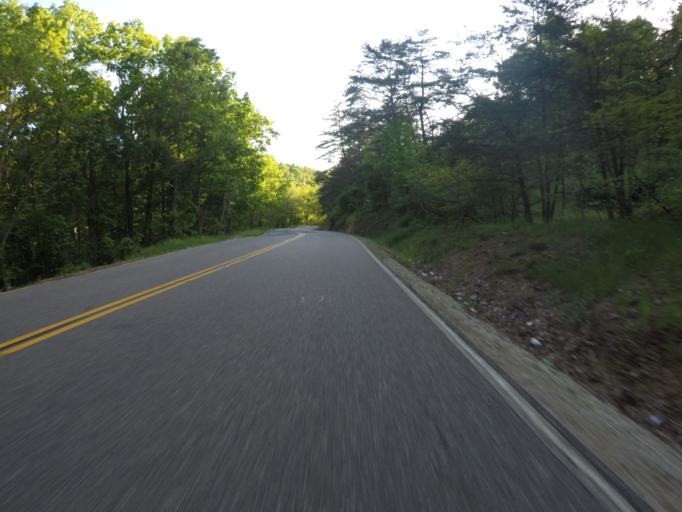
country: US
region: West Virginia
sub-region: Cabell County
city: Huntington
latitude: 38.5531
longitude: -82.4291
